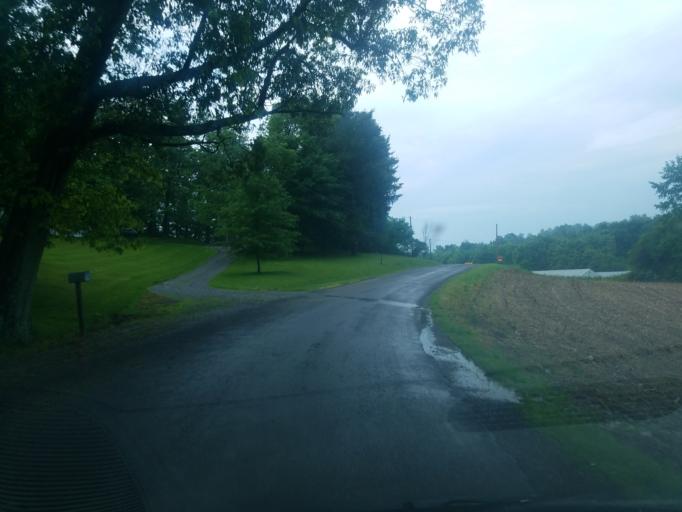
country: US
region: Ohio
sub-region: Stark County
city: Minerva
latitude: 40.7564
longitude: -80.9479
